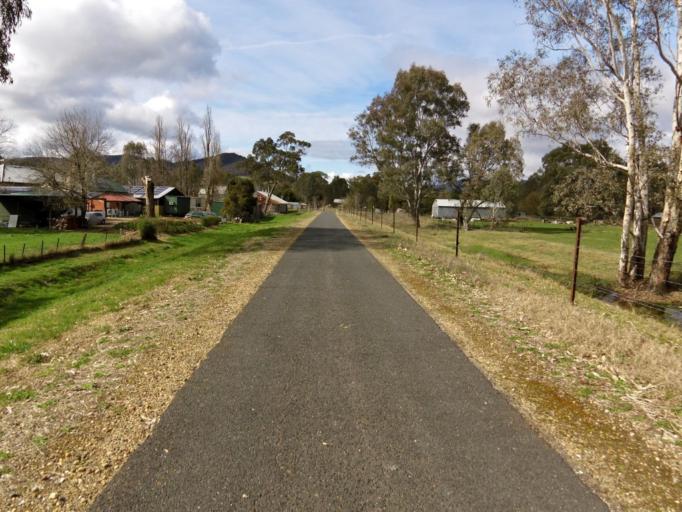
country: AU
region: Victoria
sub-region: Alpine
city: Mount Beauty
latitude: -36.5866
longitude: 146.7579
